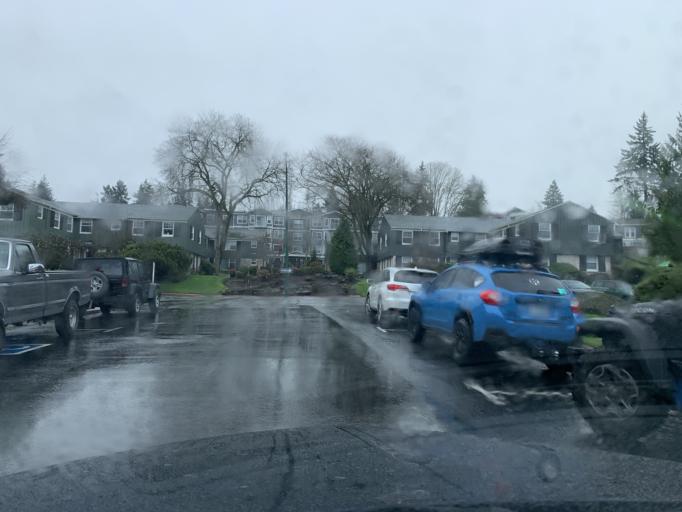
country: US
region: Washington
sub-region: King County
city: Mercer Island
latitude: 47.5802
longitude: -122.2194
